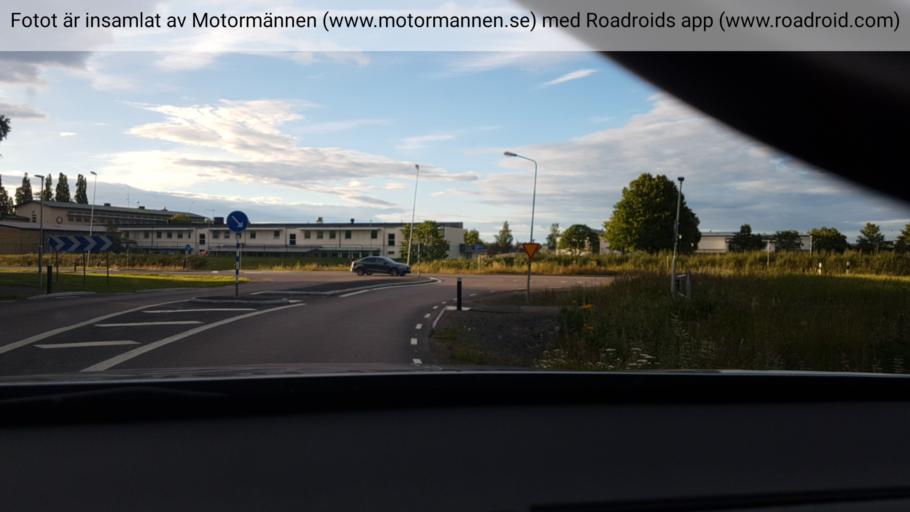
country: SE
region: Vaermland
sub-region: Sunne Kommun
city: Sunne
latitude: 59.8390
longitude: 13.1591
